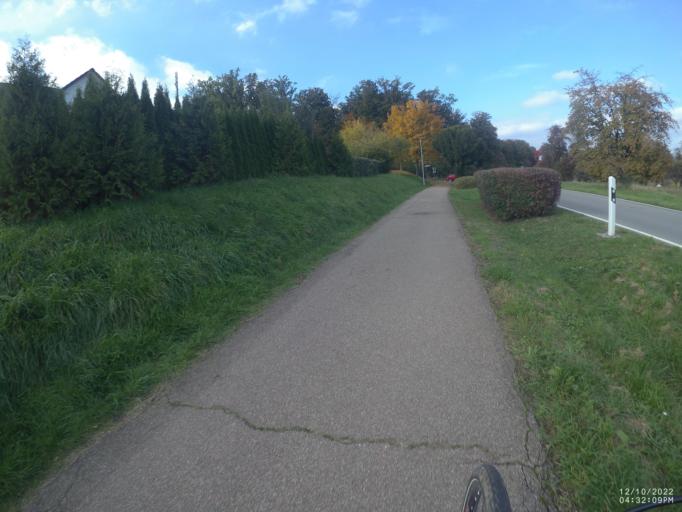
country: DE
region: Baden-Wuerttemberg
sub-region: Regierungsbezirk Stuttgart
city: Albershausen
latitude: 48.6970
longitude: 9.5621
